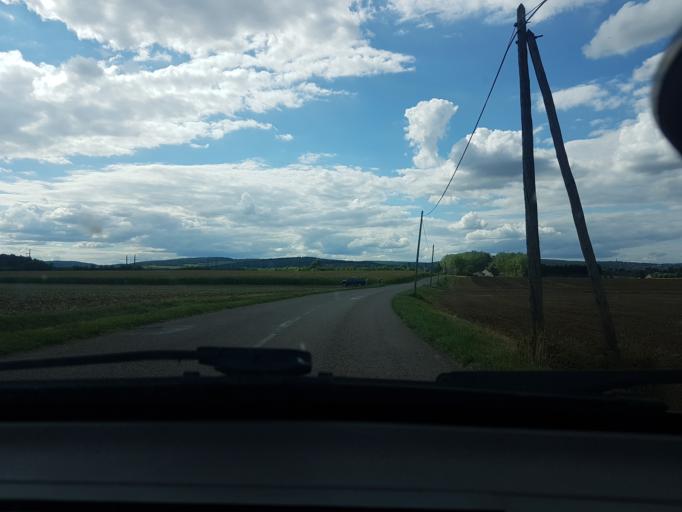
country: FR
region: Bourgogne
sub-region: Departement de Saone-et-Loire
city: Fontaines
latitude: 46.8433
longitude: 4.7875
